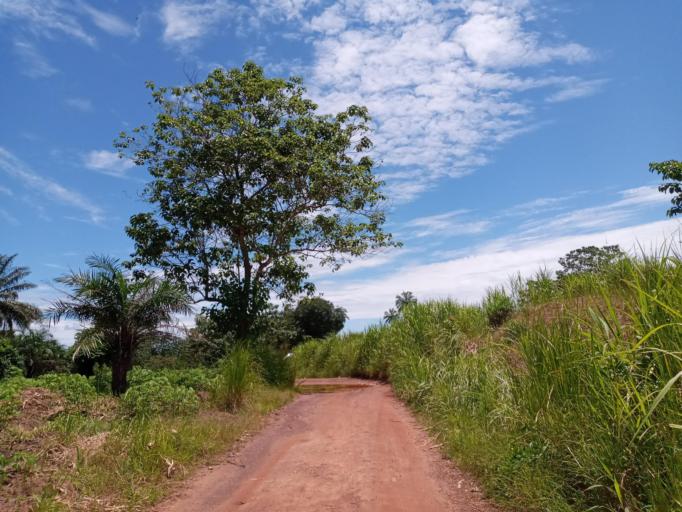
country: SL
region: Eastern Province
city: Koidu
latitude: 8.6539
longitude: -10.9467
